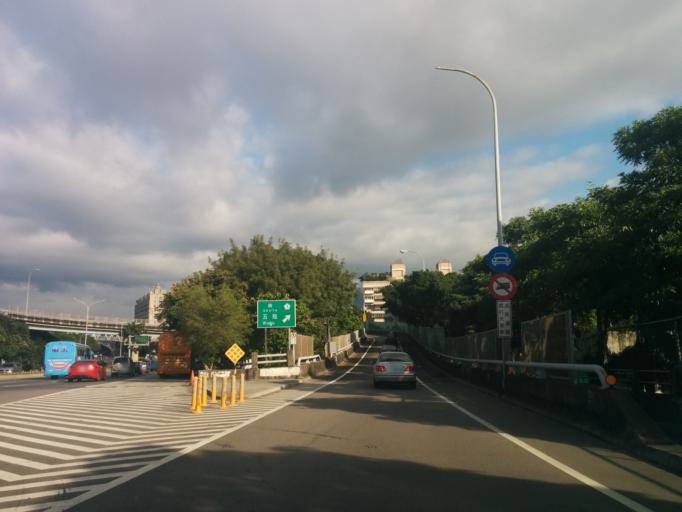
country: TW
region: Taipei
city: Taipei
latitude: 25.0807
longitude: 121.5081
